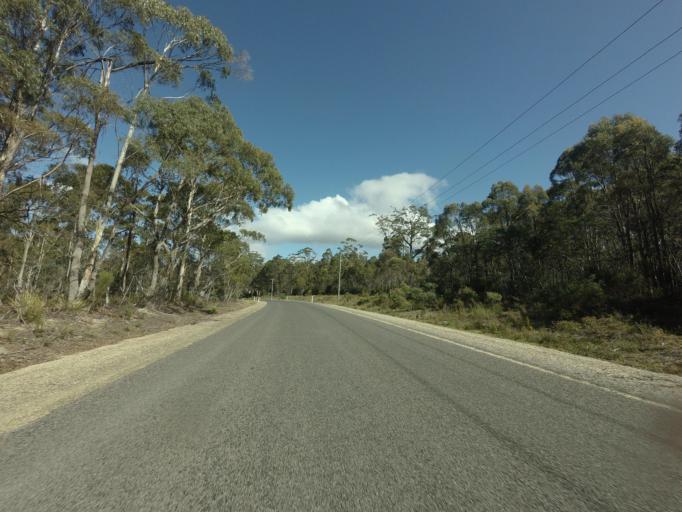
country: AU
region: Tasmania
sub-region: Break O'Day
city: St Helens
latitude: -41.6151
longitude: 148.2141
